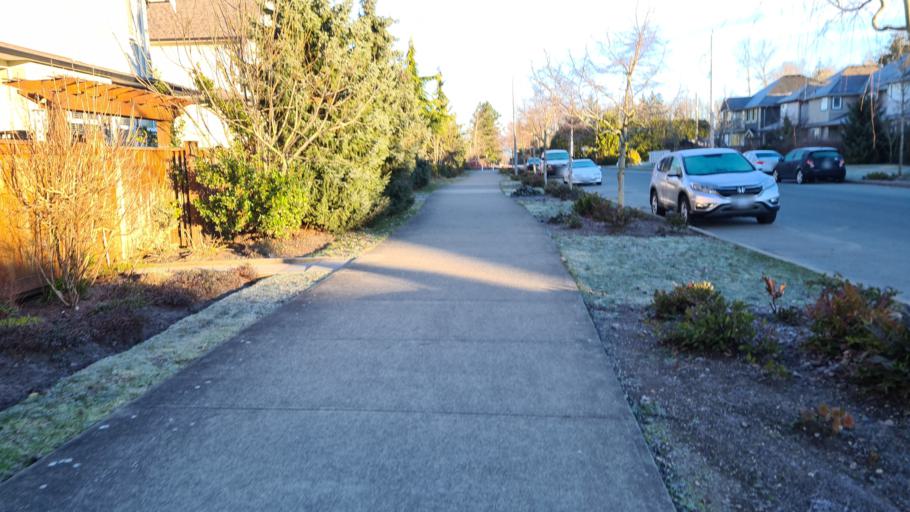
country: CA
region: British Columbia
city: Langley
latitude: 49.1347
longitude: -122.6724
